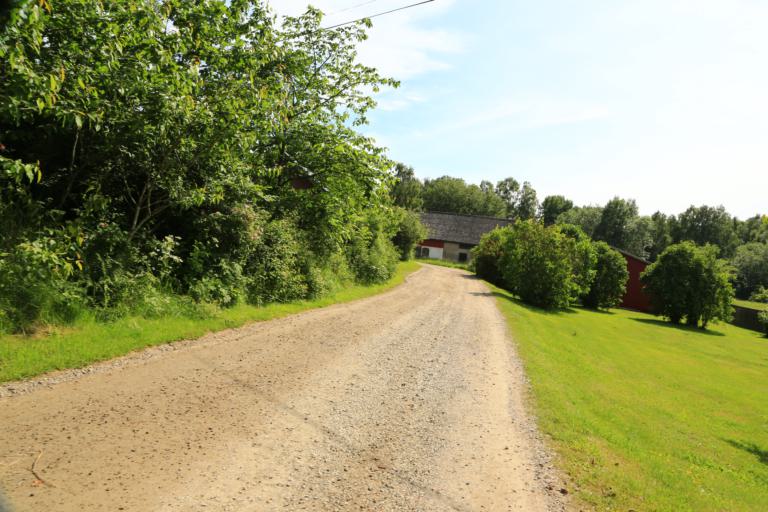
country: SE
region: Halland
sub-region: Varbergs Kommun
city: Traslovslage
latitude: 57.0939
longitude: 12.2846
